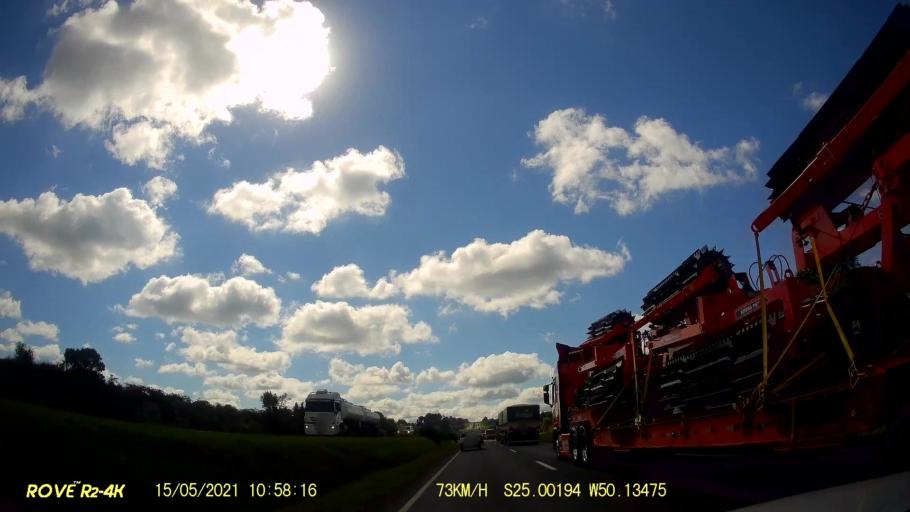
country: BR
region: Parana
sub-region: Carambei
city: Carambei
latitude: -25.0021
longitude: -50.1349
